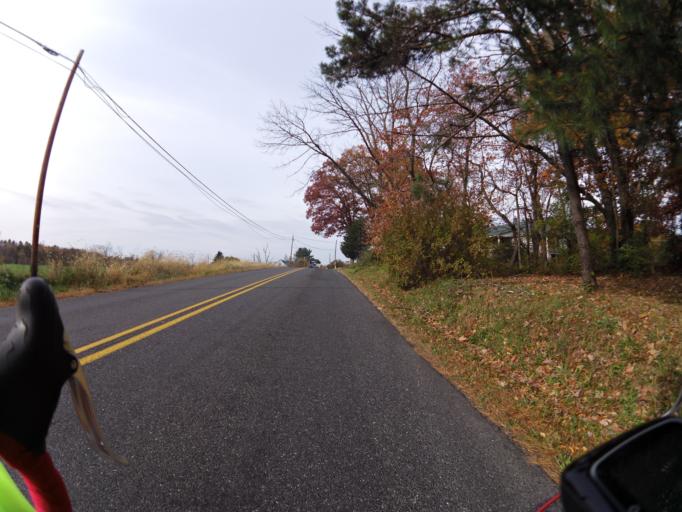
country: US
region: Pennsylvania
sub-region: Union County
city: New Columbia
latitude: 41.0515
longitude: -76.9269
